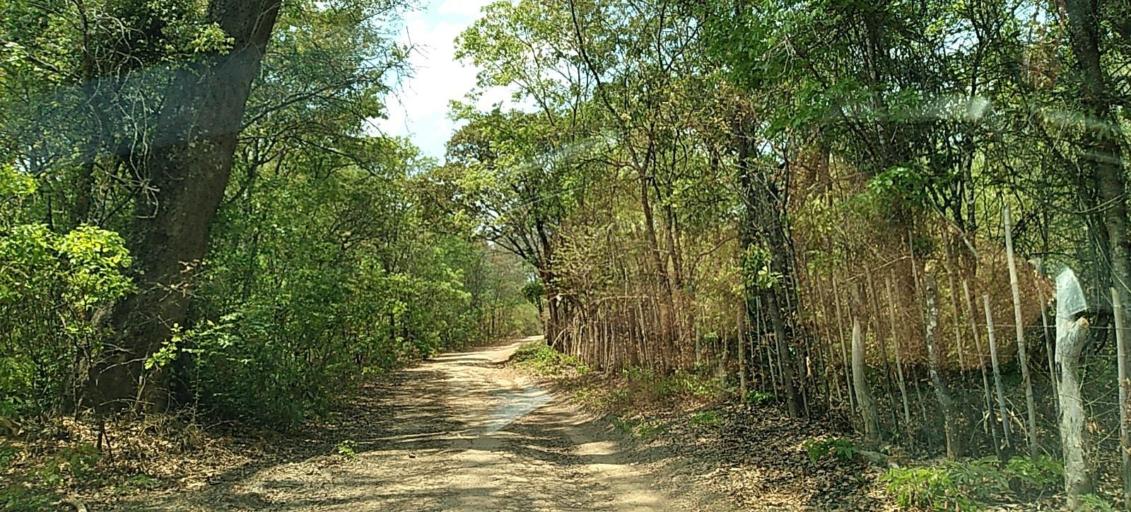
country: ZM
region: Copperbelt
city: Chililabombwe
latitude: -12.4860
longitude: 27.6405
